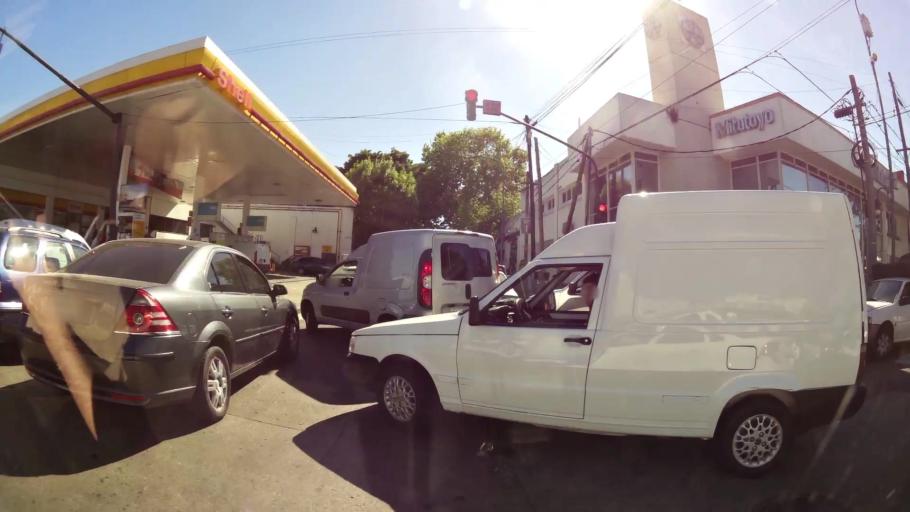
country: AR
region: Buenos Aires
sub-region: Partido de General San Martin
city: General San Martin
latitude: -34.5416
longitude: -58.5059
